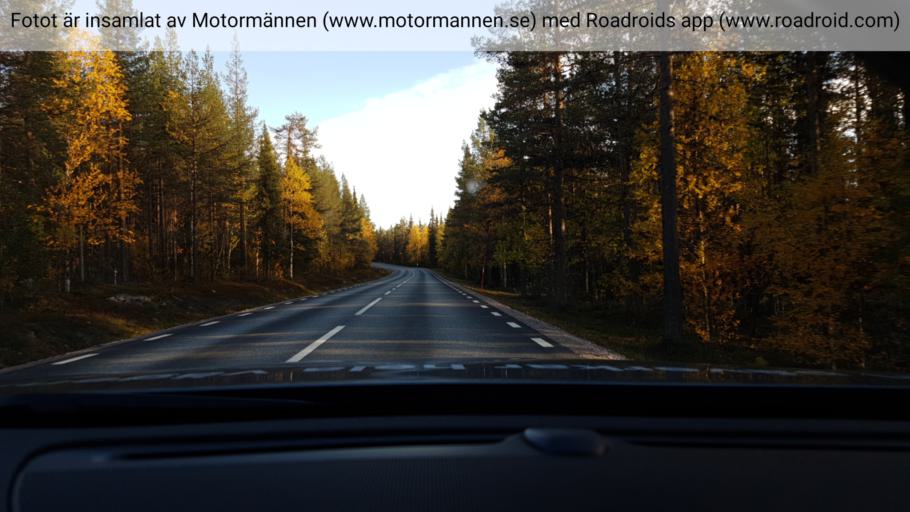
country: SE
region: Norrbotten
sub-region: Jokkmokks Kommun
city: Jokkmokk
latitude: 66.9420
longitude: 19.8019
